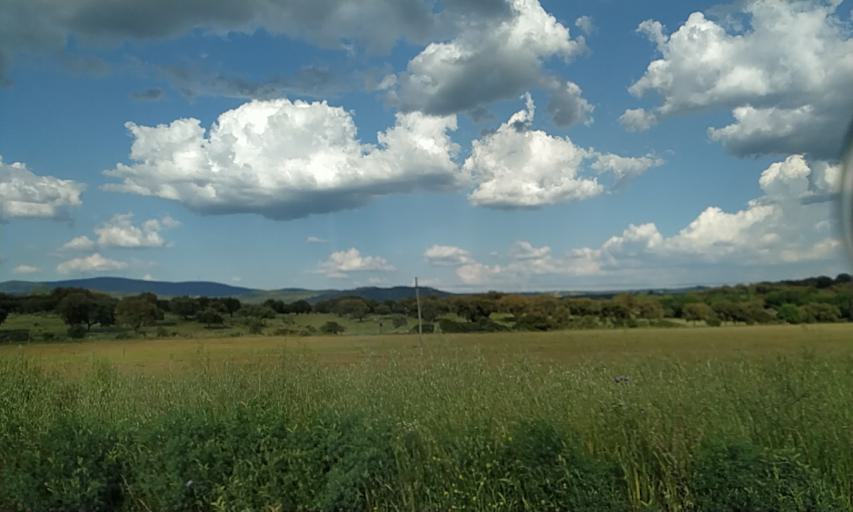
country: PT
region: Portalegre
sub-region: Portalegre
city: Portalegre
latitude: 39.2525
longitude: -7.4479
